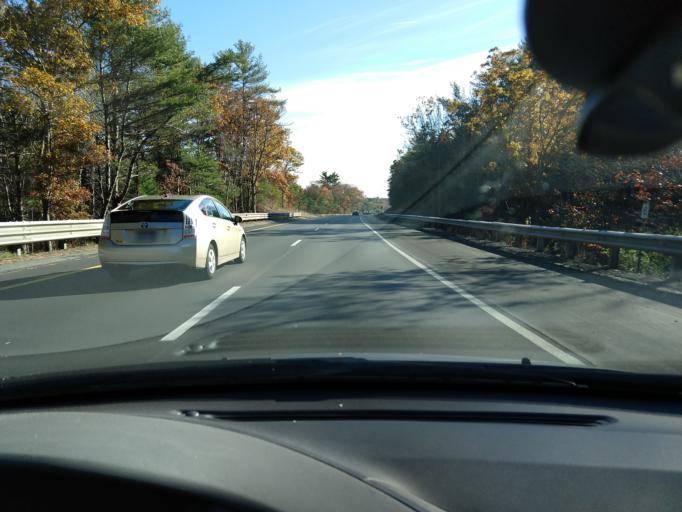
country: US
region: Massachusetts
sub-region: Plymouth County
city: Plymouth
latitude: 41.9255
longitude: -70.6309
